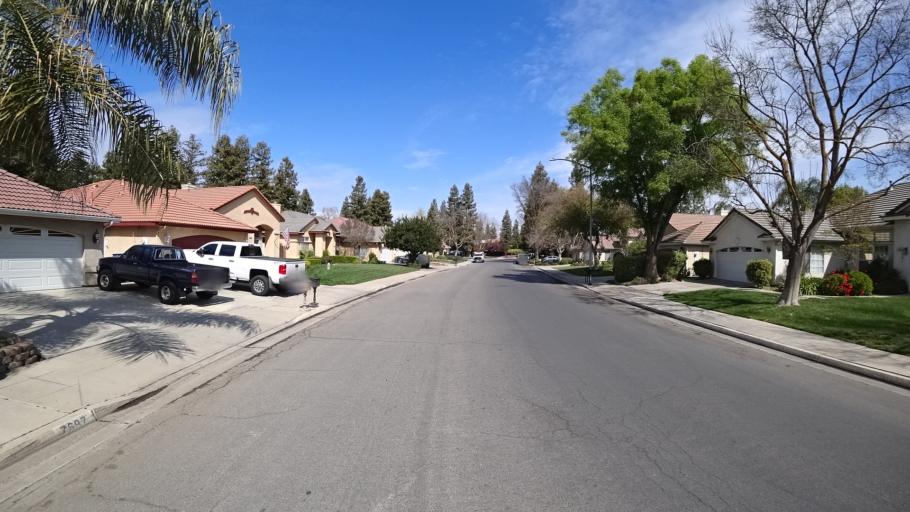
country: US
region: California
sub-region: Fresno County
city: Biola
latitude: 36.8478
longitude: -119.8877
